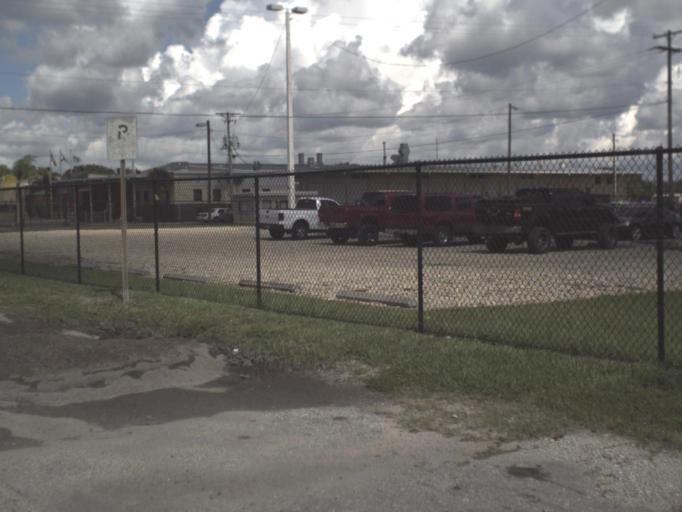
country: US
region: Florida
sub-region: Hillsborough County
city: East Lake-Orient Park
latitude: 27.9668
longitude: -82.3907
